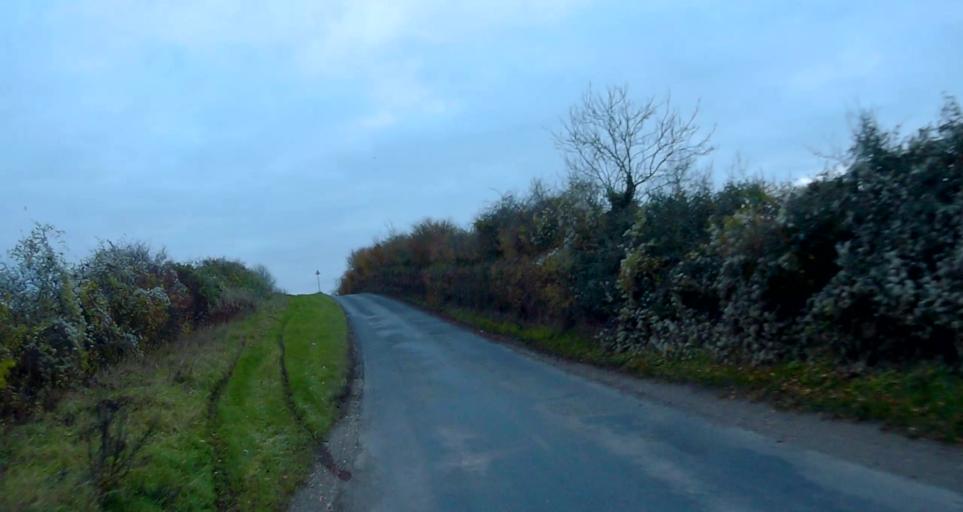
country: GB
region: England
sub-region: Hampshire
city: Odiham
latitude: 51.2468
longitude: -0.9706
